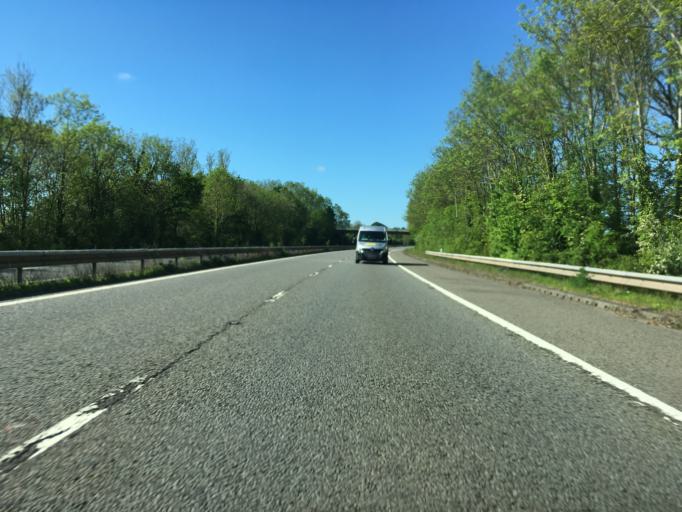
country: GB
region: England
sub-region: Herefordshire
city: Donnington
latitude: 51.9769
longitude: -2.4134
